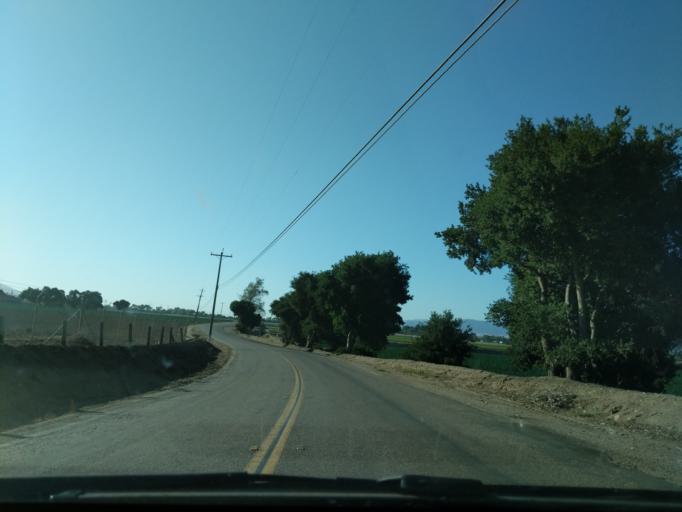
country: US
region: California
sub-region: Monterey County
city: Gonzales
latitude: 36.4696
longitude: -121.4692
